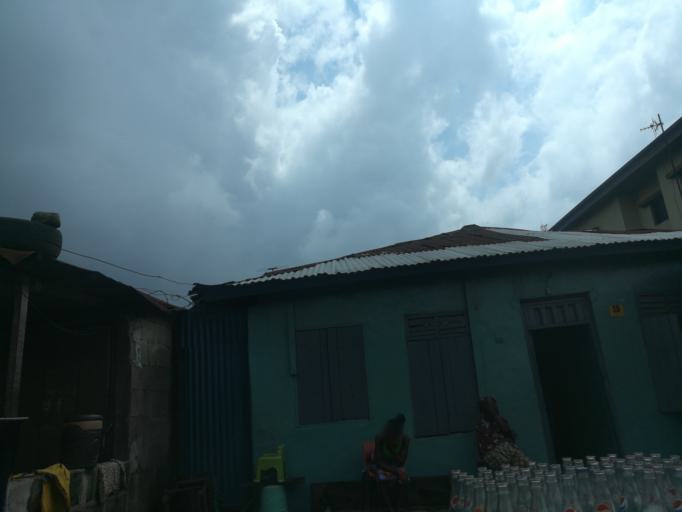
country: NG
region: Lagos
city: Mushin
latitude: 6.5285
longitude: 3.3644
